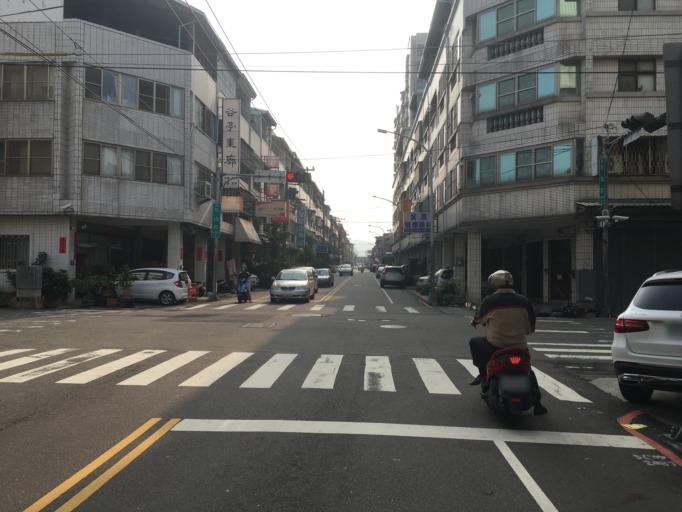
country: TW
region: Taiwan
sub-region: Taichung City
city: Taichung
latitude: 24.1866
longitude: 120.6982
